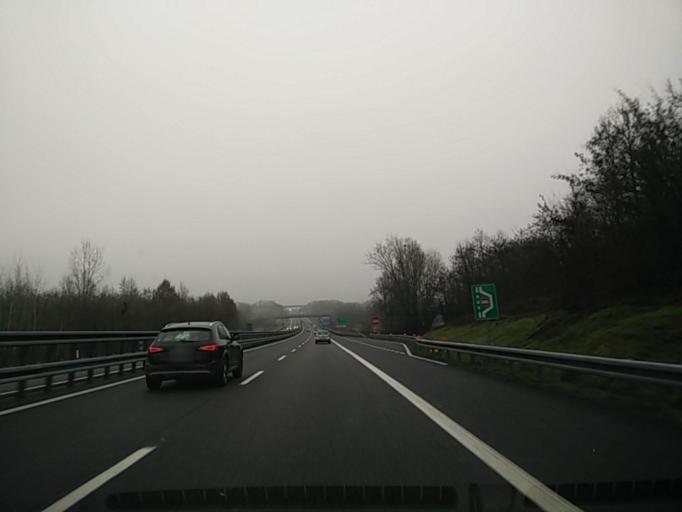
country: IT
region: Piedmont
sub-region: Provincia di Alessandria
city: Quattordio
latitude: 44.9069
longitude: 8.3939
